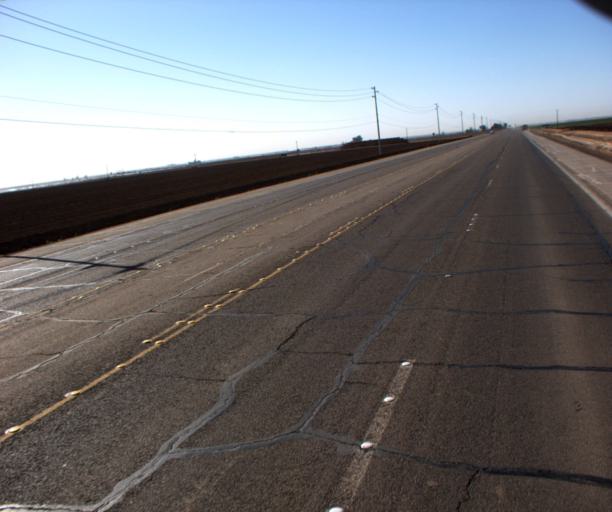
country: US
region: Arizona
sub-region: Yuma County
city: Somerton
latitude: 32.5853
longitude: -114.7699
